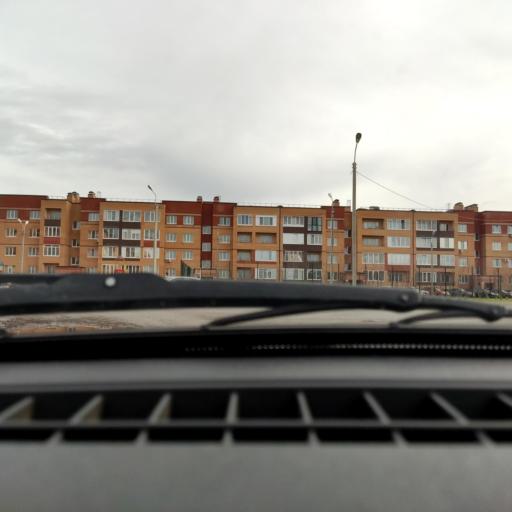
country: RU
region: Bashkortostan
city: Ufa
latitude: 54.6213
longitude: 55.8818
